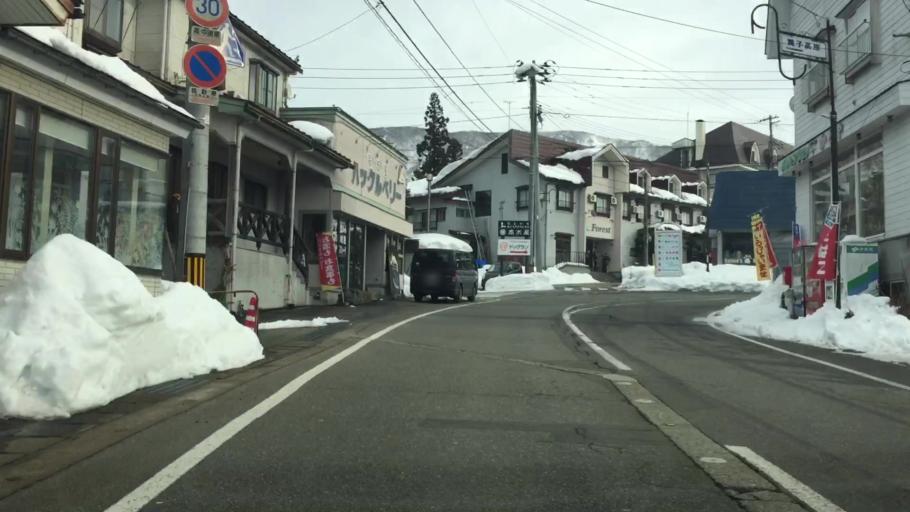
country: JP
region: Niigata
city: Shiozawa
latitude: 36.9904
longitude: 138.8225
